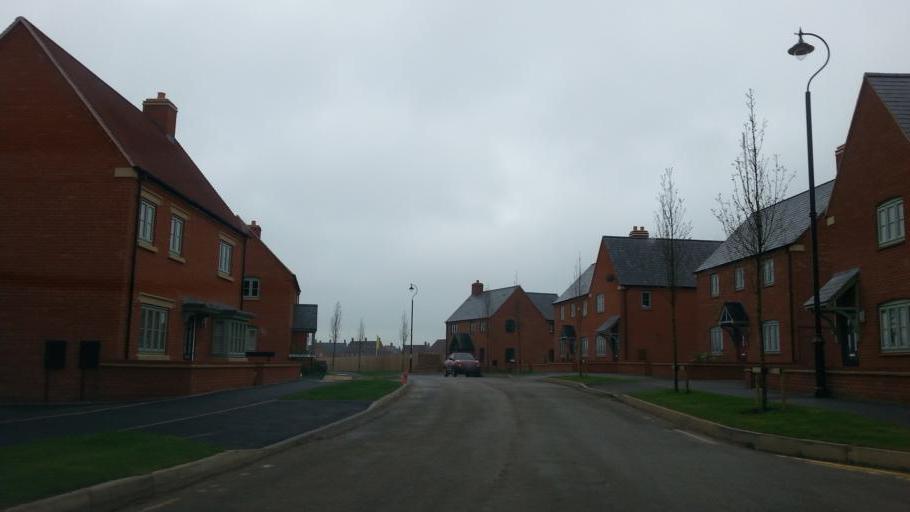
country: GB
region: England
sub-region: Northamptonshire
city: Brackley
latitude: 52.0461
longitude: -1.1505
